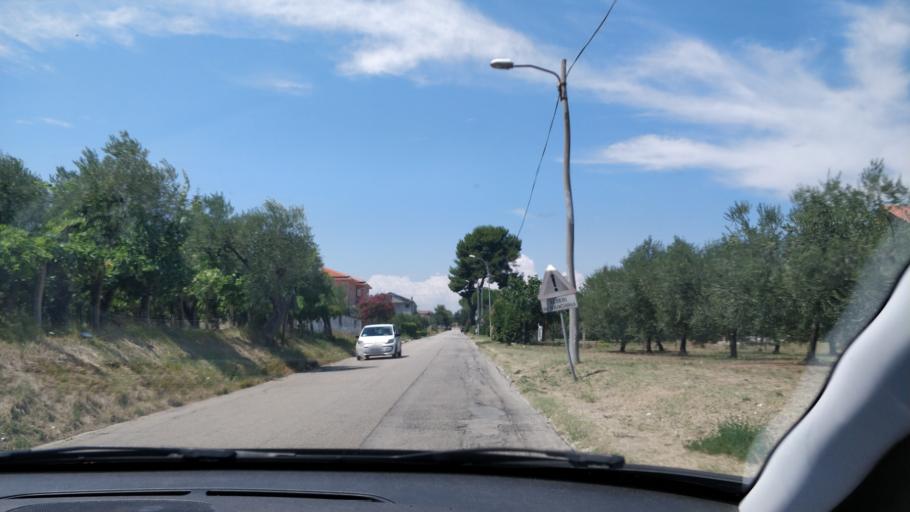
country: IT
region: Abruzzo
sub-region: Provincia di Chieti
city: Francavilla al Mare
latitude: 42.4229
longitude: 14.2632
